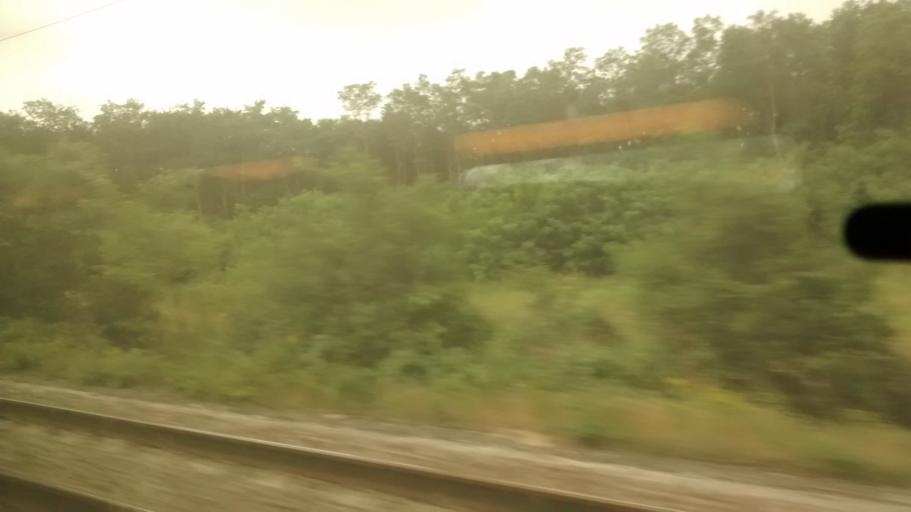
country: FR
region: Bourgogne
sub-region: Departement de l'Yonne
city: Vergigny
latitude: 47.9670
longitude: 3.7091
